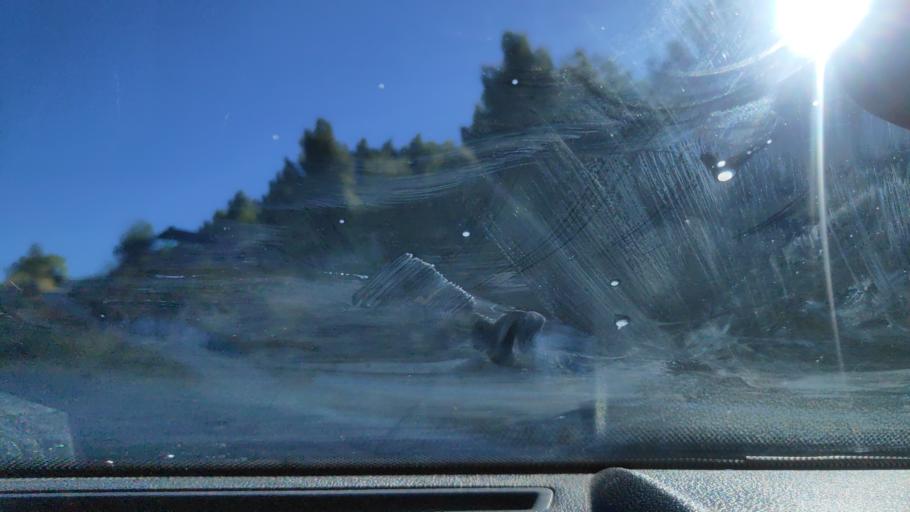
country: ES
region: Andalusia
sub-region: Provincia de Jaen
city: Jimena
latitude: 37.8396
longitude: -3.4782
